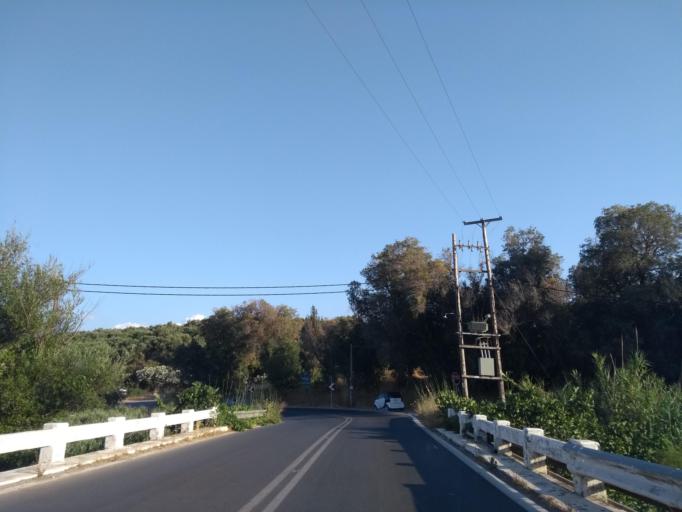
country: GR
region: Crete
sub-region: Nomos Chanias
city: Kalivai
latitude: 35.4597
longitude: 24.1536
